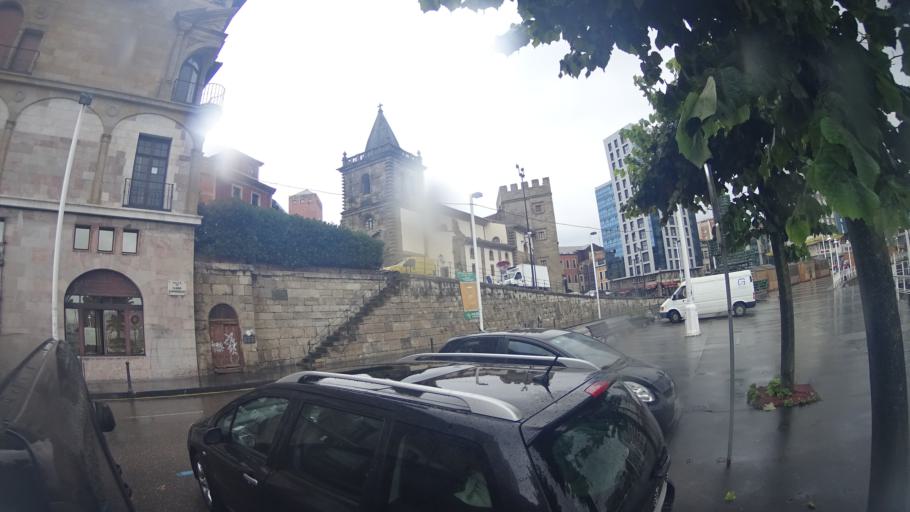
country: ES
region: Asturias
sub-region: Province of Asturias
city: Gijon
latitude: 43.5456
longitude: -5.6646
